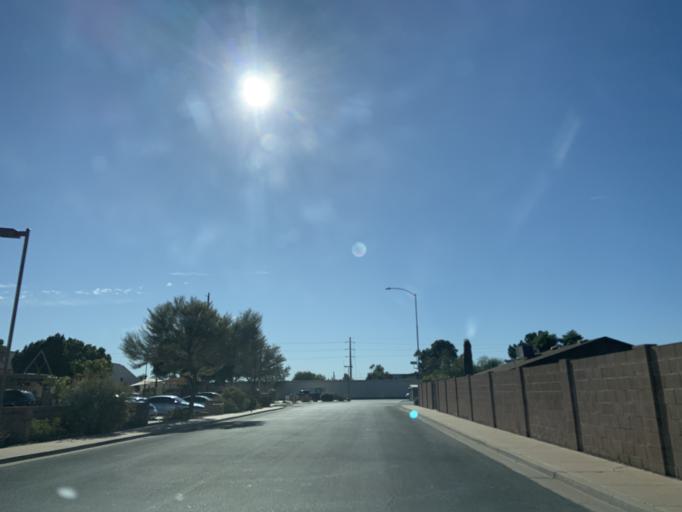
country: US
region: Arizona
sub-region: Maricopa County
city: San Carlos
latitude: 33.3661
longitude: -111.8618
